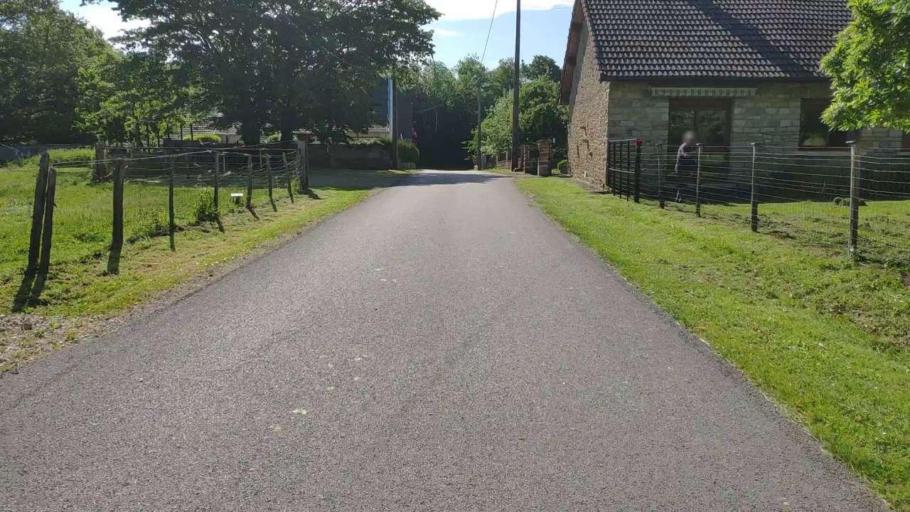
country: FR
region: Franche-Comte
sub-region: Departement du Jura
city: Montmorot
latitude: 46.6960
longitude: 5.4775
